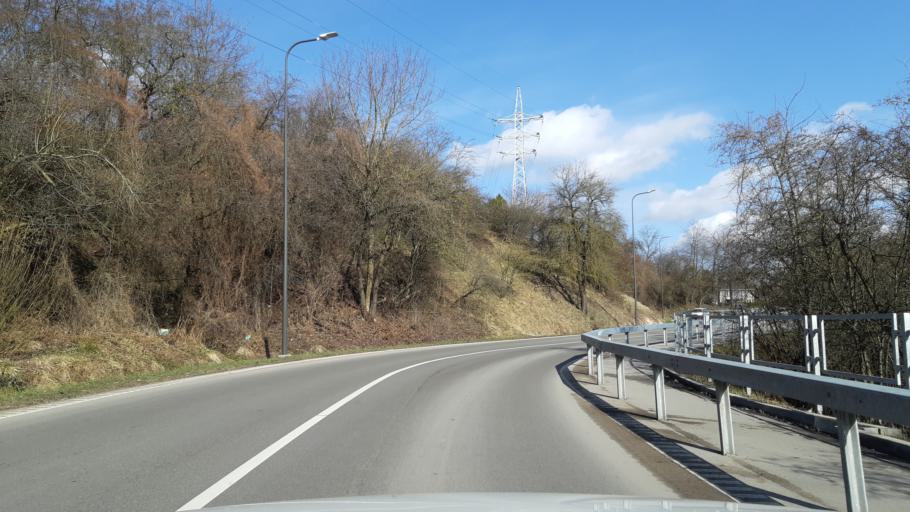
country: LT
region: Kauno apskritis
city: Dainava (Kaunas)
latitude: 54.8921
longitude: 23.9579
